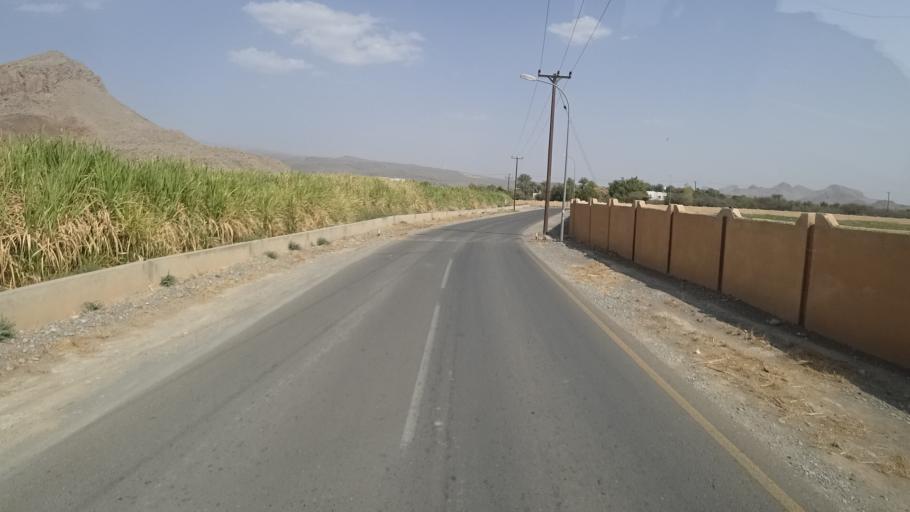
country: OM
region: Muhafazat ad Dakhiliyah
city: Bahla'
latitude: 23.1067
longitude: 57.2981
